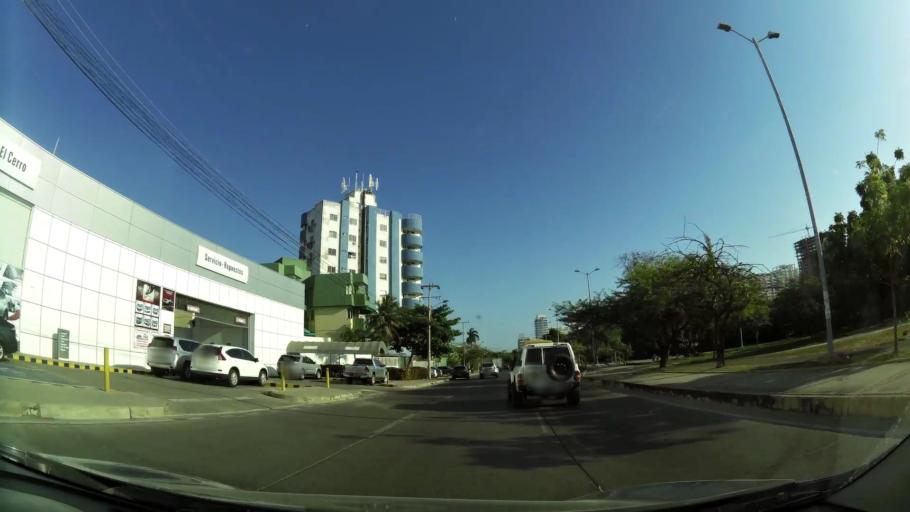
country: CO
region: Bolivar
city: Cartagena
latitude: 10.4196
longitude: -75.5361
